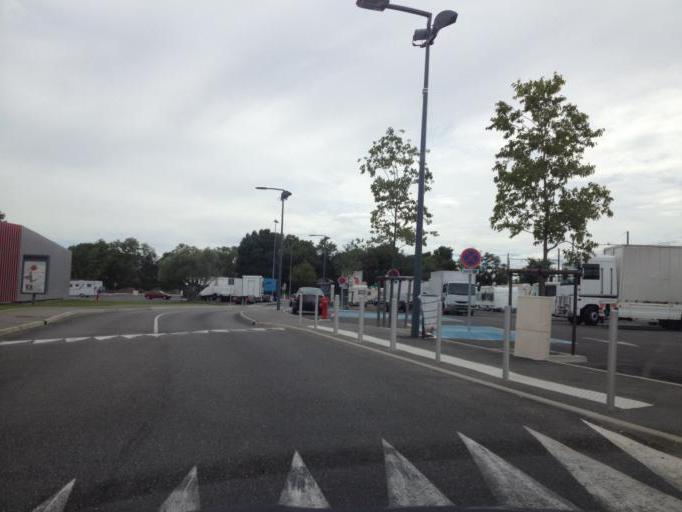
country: FR
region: Rhone-Alpes
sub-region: Departement de la Drome
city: Montelimar
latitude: 44.5555
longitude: 4.7442
